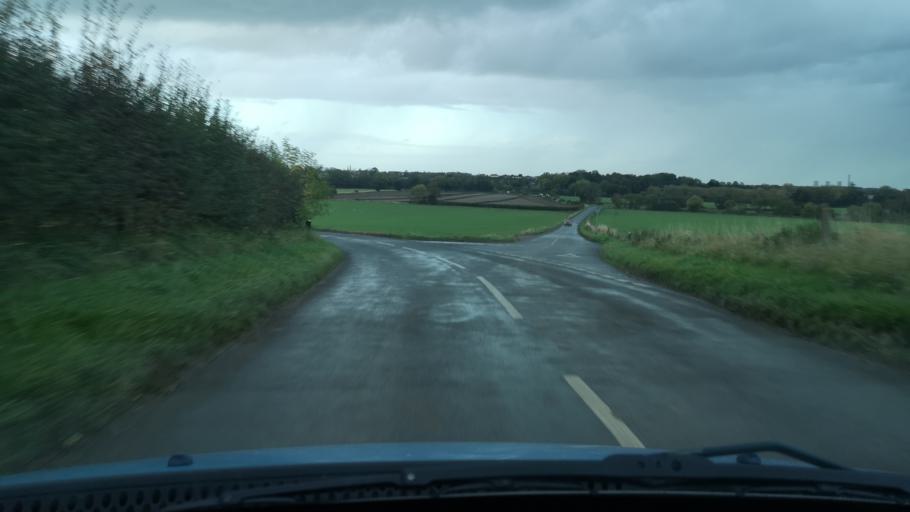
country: GB
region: England
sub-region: Doncaster
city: Norton
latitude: 53.6335
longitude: -1.2019
